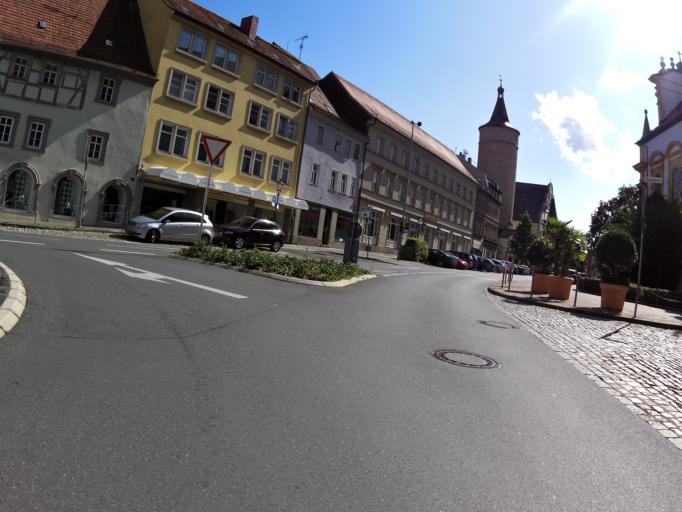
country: DE
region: Bavaria
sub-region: Regierungsbezirk Unterfranken
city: Kitzingen
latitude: 49.7401
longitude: 10.1625
